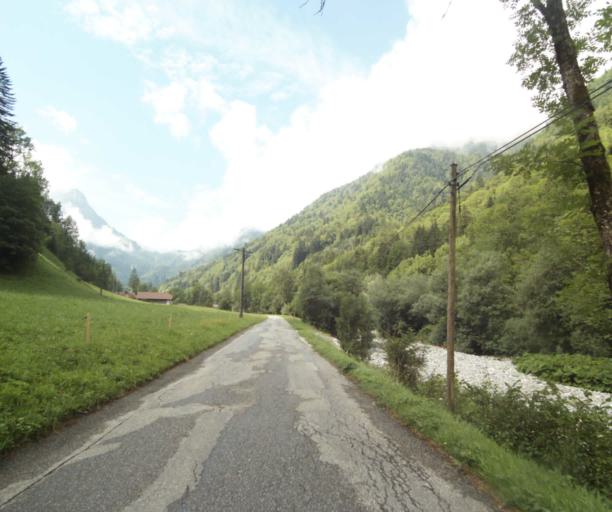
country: FR
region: Rhone-Alpes
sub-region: Departement de la Haute-Savoie
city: Thones
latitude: 45.8713
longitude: 6.2891
